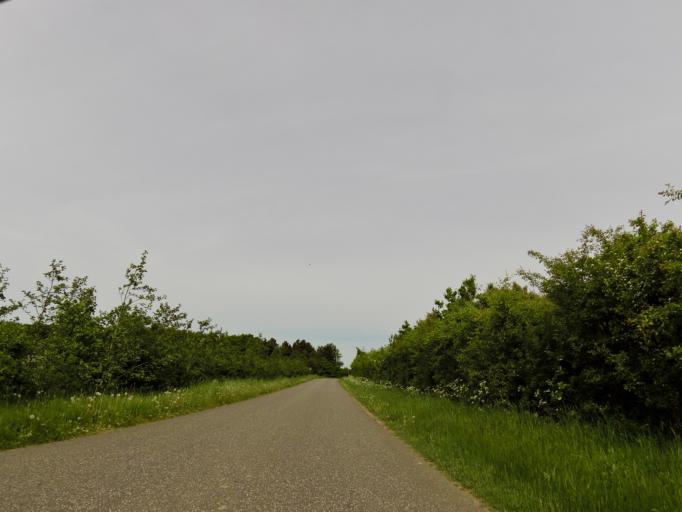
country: DK
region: Central Jutland
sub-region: Holstebro Kommune
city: Vinderup
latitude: 56.5539
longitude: 8.8905
